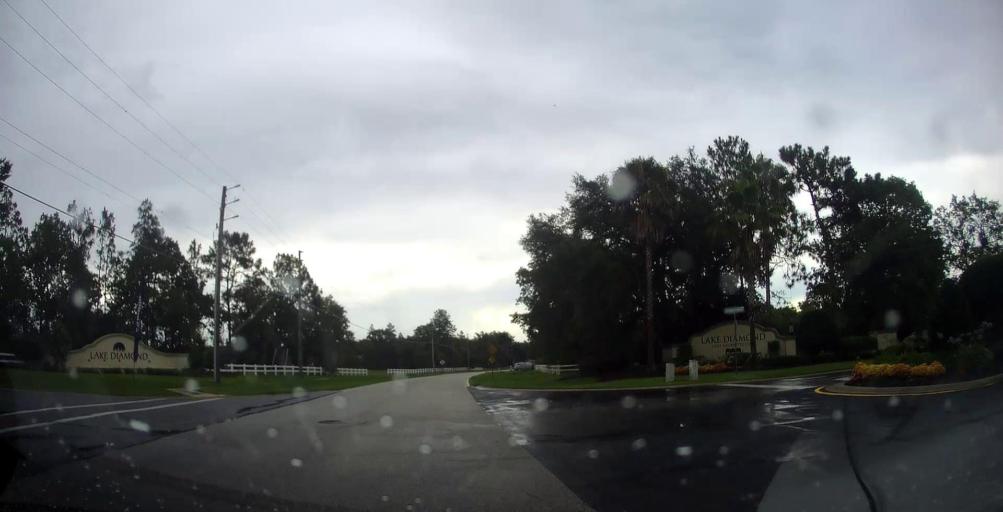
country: US
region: Florida
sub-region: Marion County
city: Silver Springs Shores
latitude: 29.1285
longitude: -82.0152
